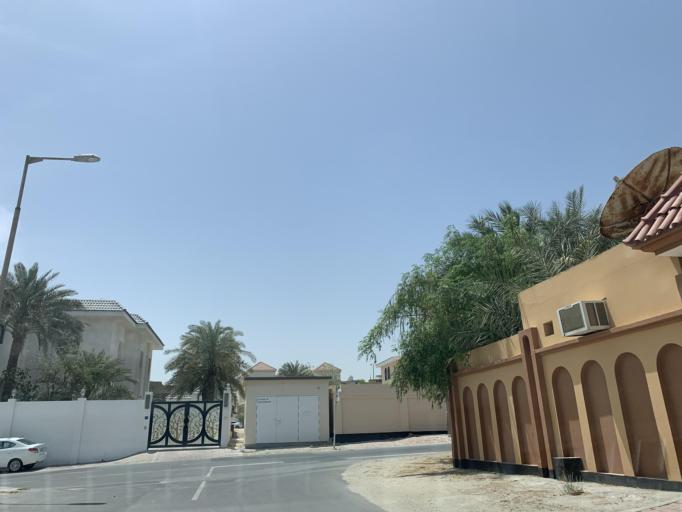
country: BH
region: Northern
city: Ar Rifa'
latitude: 26.1414
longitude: 50.5579
